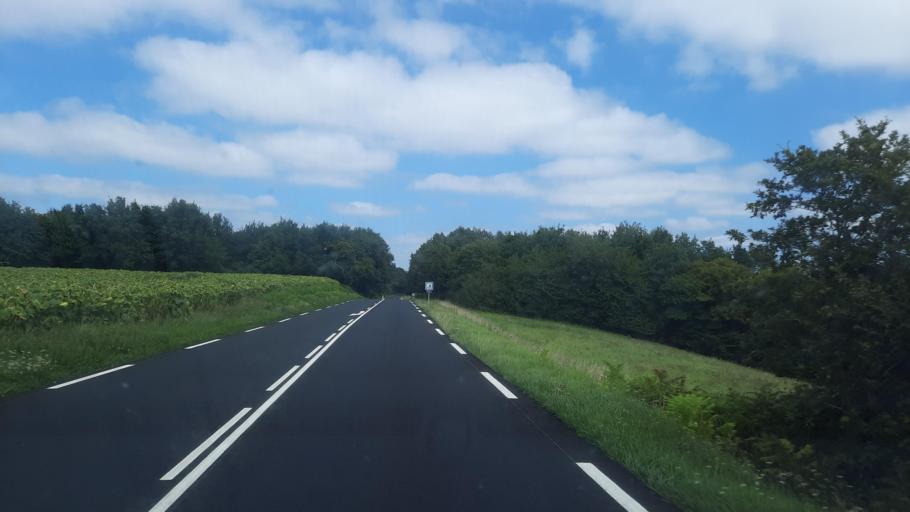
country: FR
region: Midi-Pyrenees
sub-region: Departement de la Haute-Garonne
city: Boulogne-sur-Gesse
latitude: 43.2954
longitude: 0.5846
